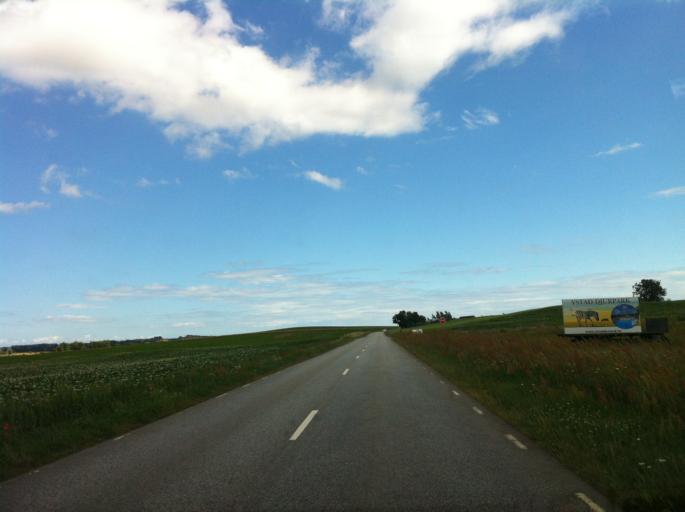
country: SE
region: Skane
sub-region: Ystads Kommun
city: Kopingebro
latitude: 55.4279
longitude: 13.9830
